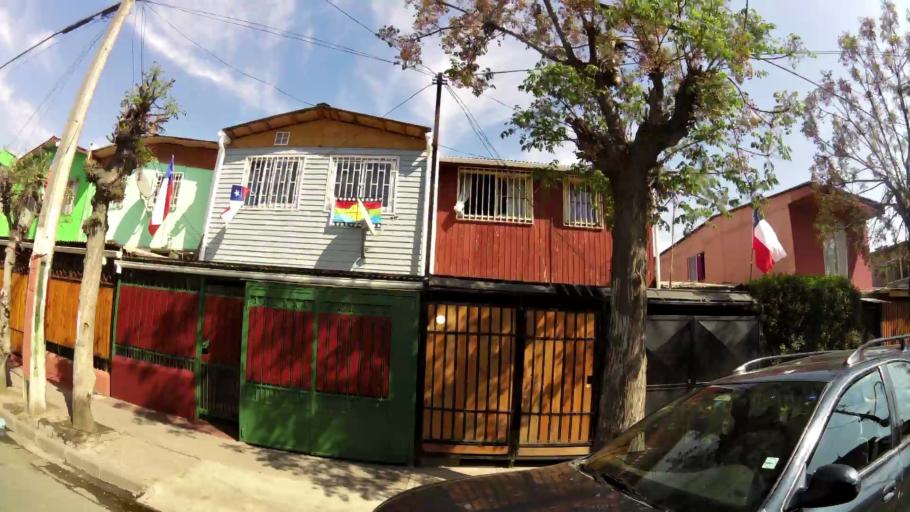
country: CL
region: Santiago Metropolitan
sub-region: Provincia de Santiago
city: La Pintana
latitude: -33.5609
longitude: -70.6519
